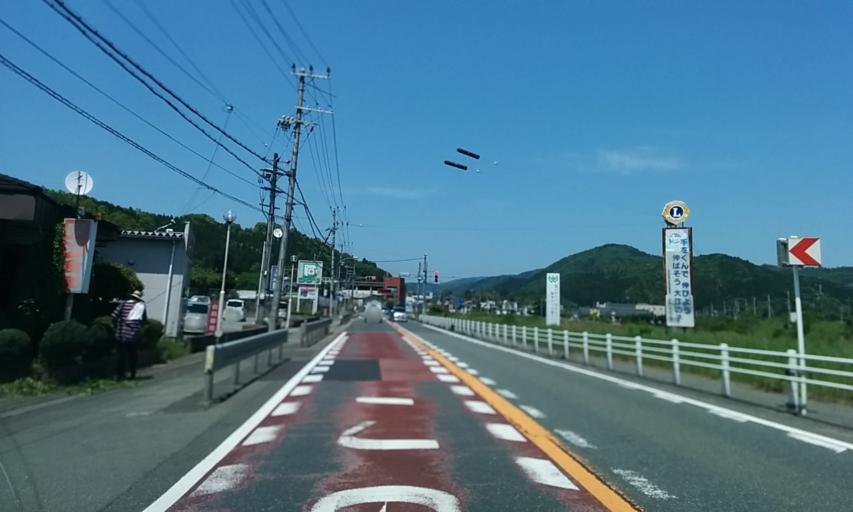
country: JP
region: Kyoto
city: Fukuchiyama
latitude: 35.3853
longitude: 135.1445
